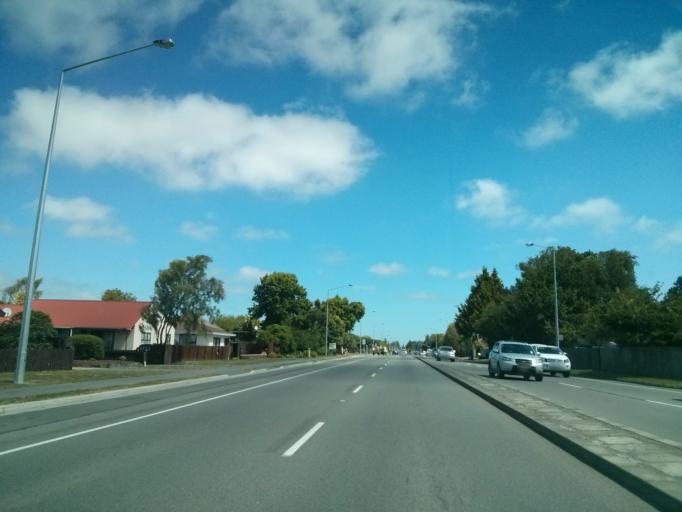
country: NZ
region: Canterbury
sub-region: Waimakariri District
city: Kaiapoi
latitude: -43.4421
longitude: 172.6344
